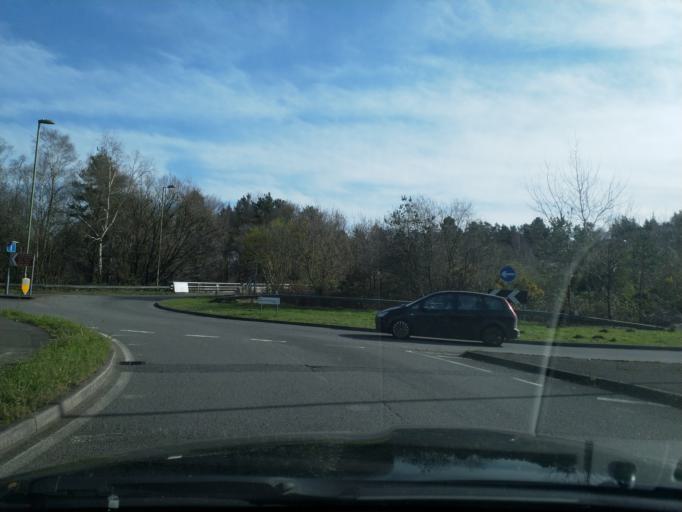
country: GB
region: England
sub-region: Hampshire
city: Fleet
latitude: 51.2758
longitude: -0.8078
